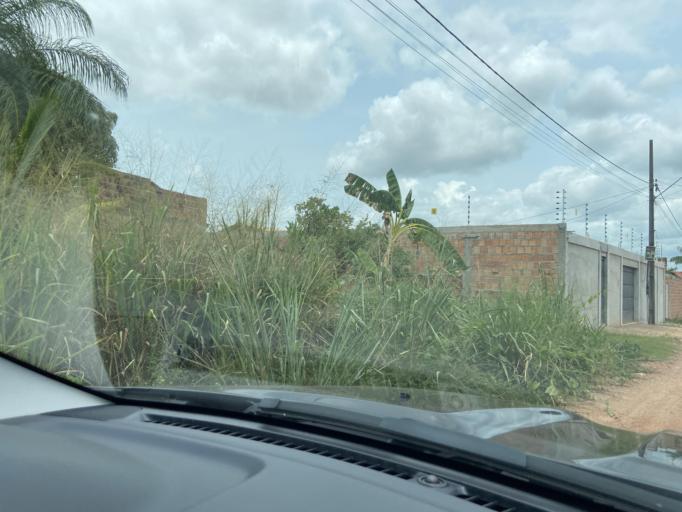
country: BR
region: Para
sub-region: Maraba
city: Maraba
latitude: -5.3549
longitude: -49.0728
